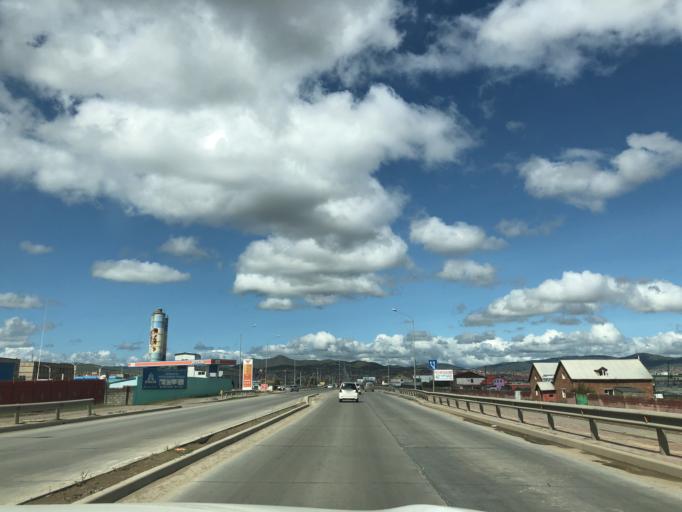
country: MN
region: Ulaanbaatar
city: Ulaanbaatar
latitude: 47.8932
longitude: 106.7854
